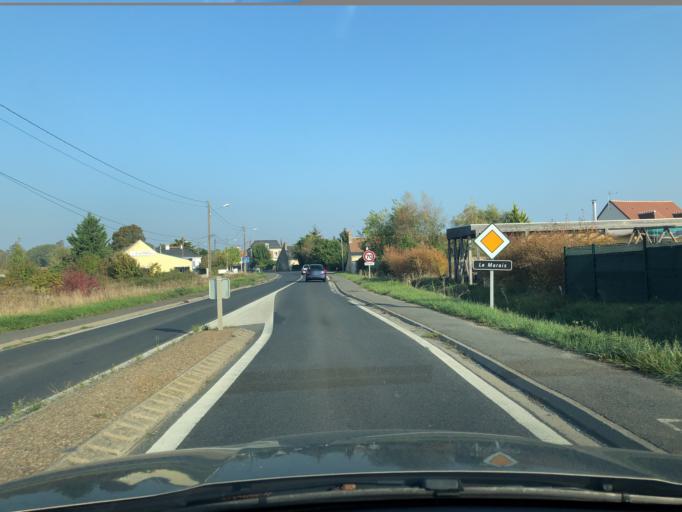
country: FR
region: Centre
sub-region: Departement d'Indre-et-Loire
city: Chanceaux-sur-Choisille
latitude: 47.4436
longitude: 0.6998
